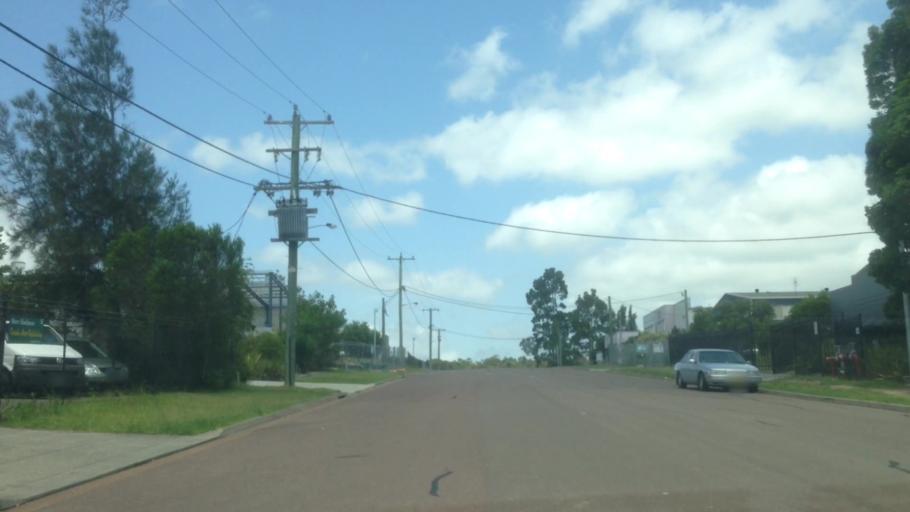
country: AU
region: New South Wales
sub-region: Lake Macquarie Shire
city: Dora Creek
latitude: -33.1193
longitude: 151.4733
